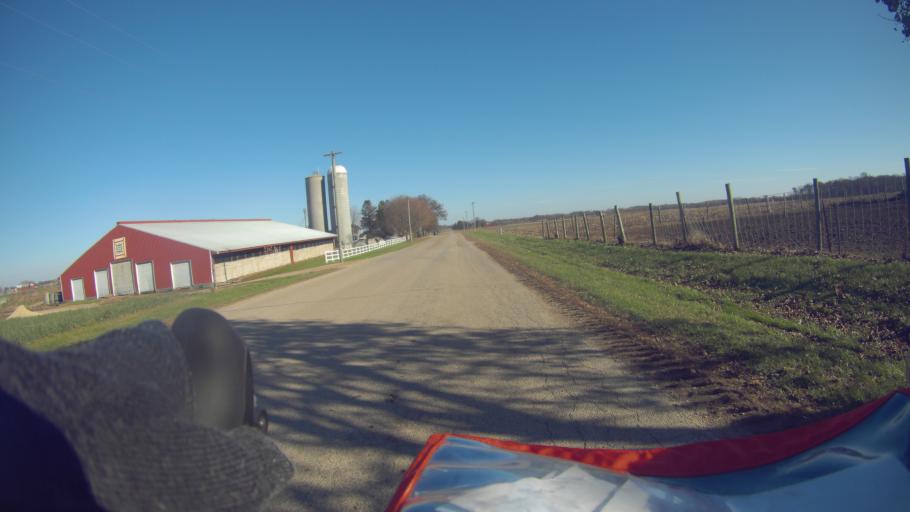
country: US
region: Wisconsin
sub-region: Dane County
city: Stoughton
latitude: 42.8824
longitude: -89.1895
